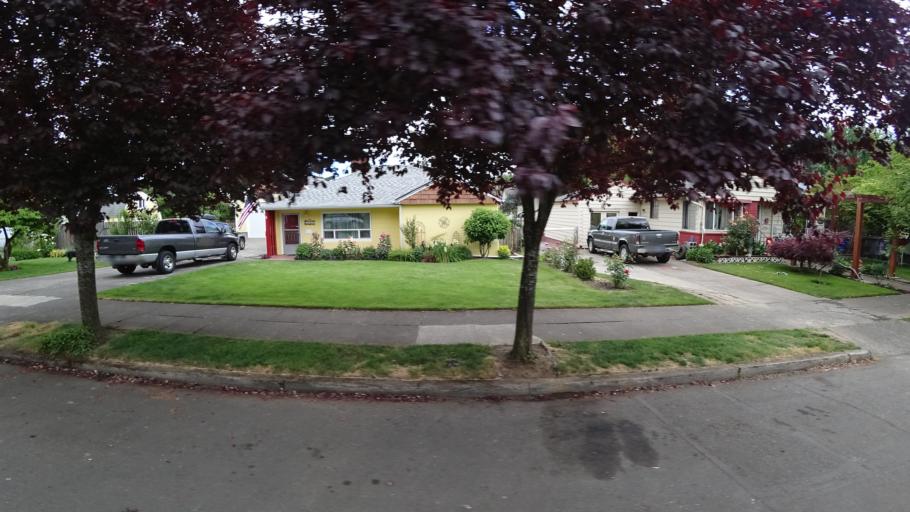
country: US
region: Oregon
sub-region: Washington County
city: West Haven
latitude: 45.5968
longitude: -122.7564
